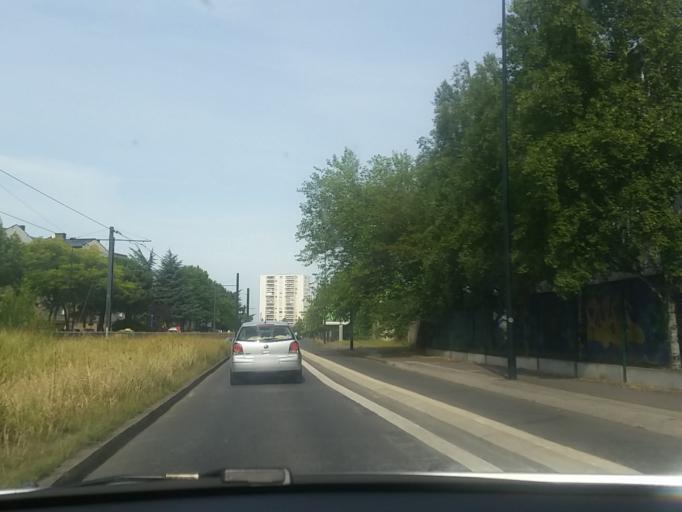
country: FR
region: Pays de la Loire
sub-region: Departement de la Loire-Atlantique
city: Bouguenais
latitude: 47.2103
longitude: -1.6038
